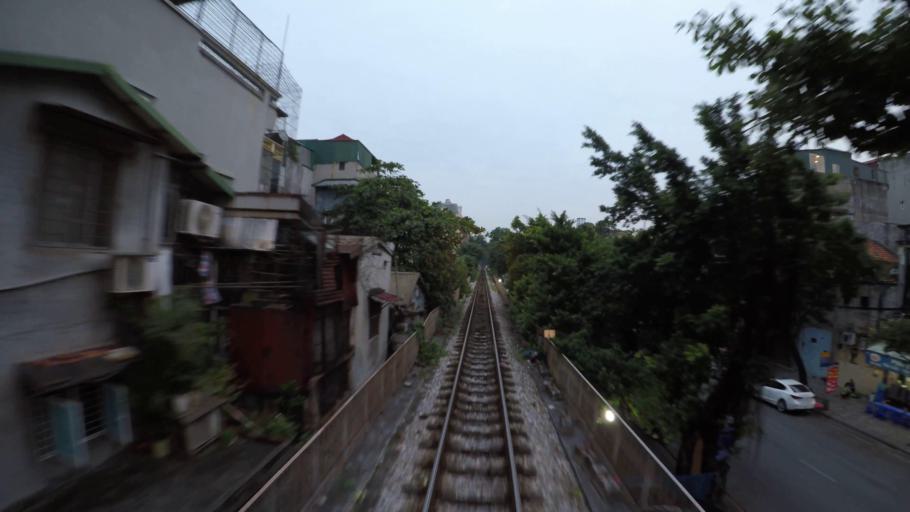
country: VN
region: Ha Noi
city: Hoan Kiem
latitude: 21.0424
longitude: 105.8562
